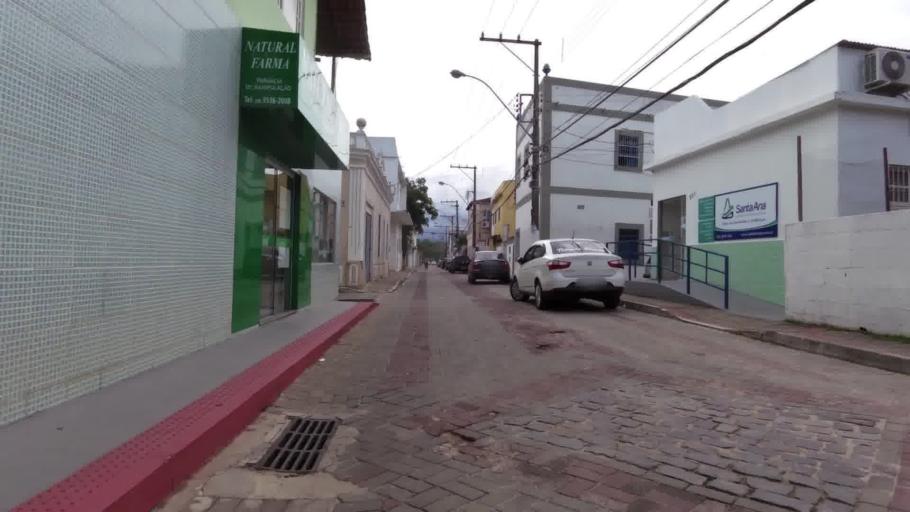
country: BR
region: Espirito Santo
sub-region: Piuma
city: Piuma
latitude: -20.8050
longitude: -40.6542
